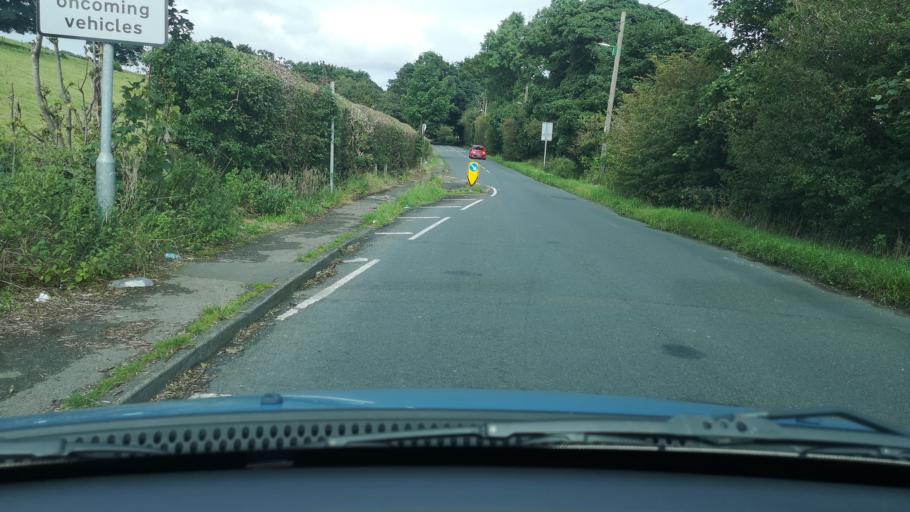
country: GB
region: England
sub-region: Kirklees
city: Heckmondwike
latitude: 53.7260
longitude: -1.6710
